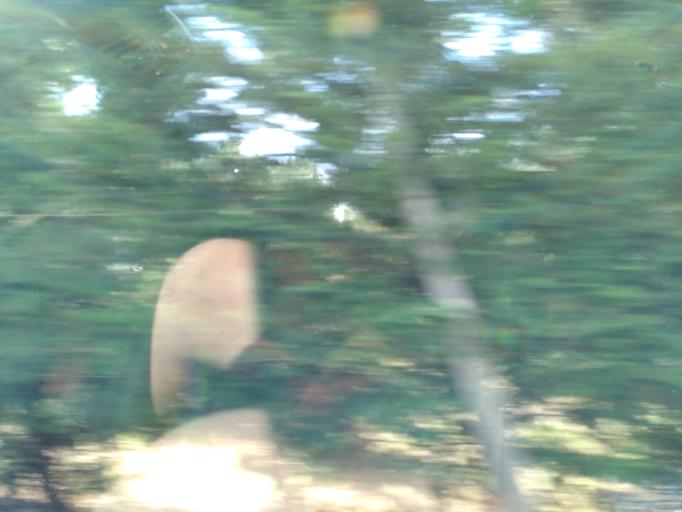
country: GR
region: Central Macedonia
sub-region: Nomos Thessalonikis
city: Agia Triada
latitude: 40.4925
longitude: 22.8615
